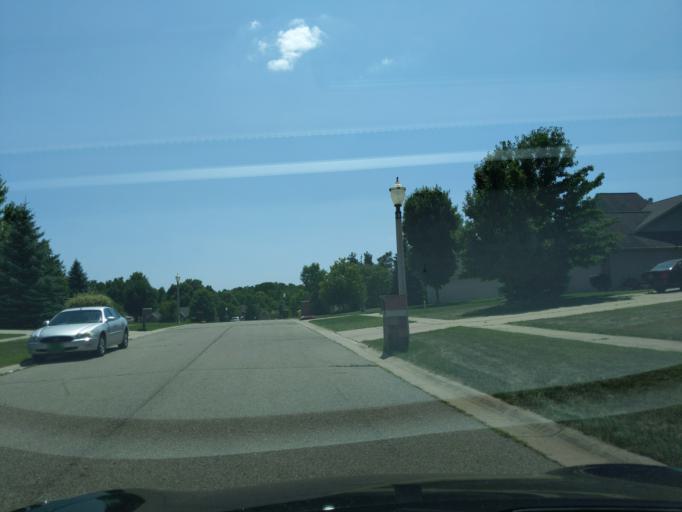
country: US
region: Michigan
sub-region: Ingham County
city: Edgemont Park
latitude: 42.7658
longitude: -84.6072
